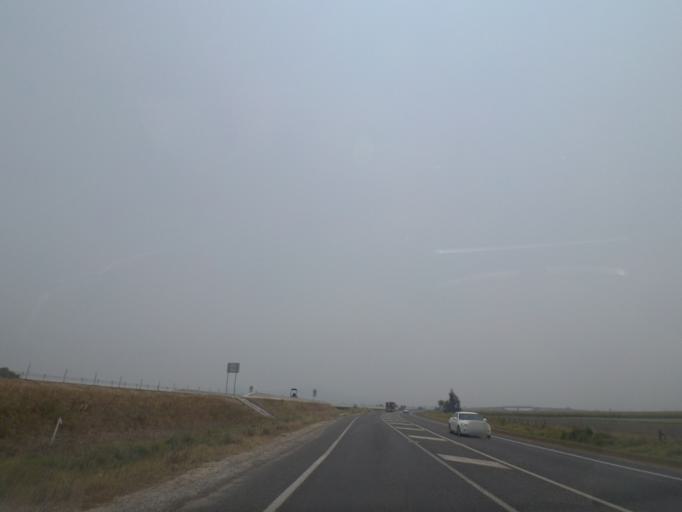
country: AU
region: New South Wales
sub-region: Clarence Valley
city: Maclean
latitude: -29.4006
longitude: 153.2408
